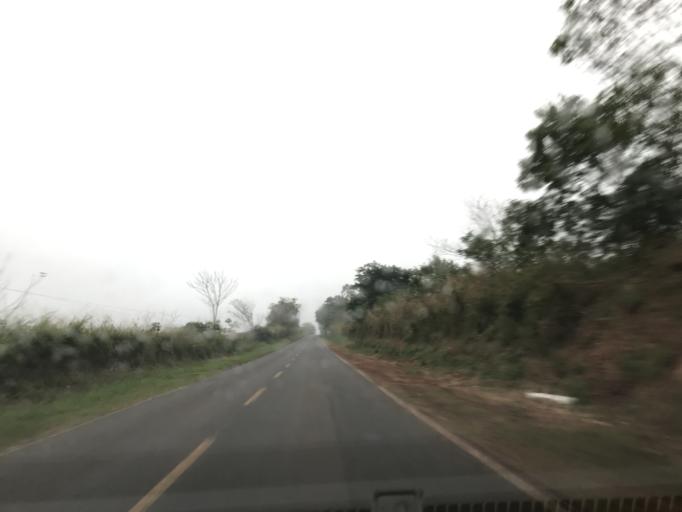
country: PY
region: Canindeyu
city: Salto del Guaira
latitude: -24.1062
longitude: -54.1070
